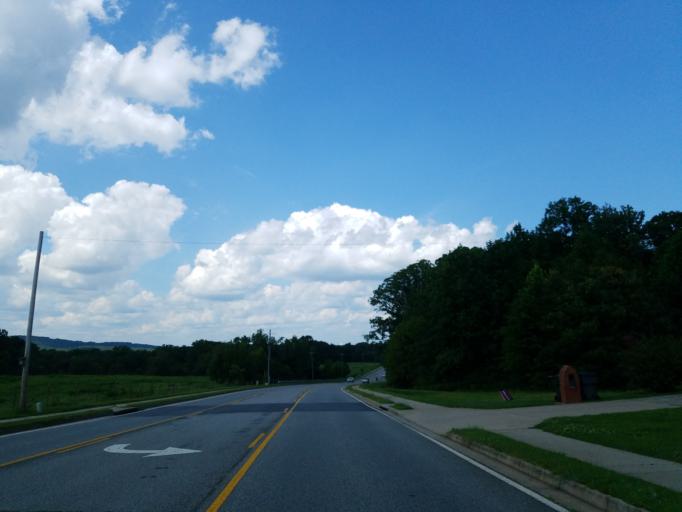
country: US
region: Georgia
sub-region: Forsyth County
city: Cumming
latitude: 34.2164
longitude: -84.1266
